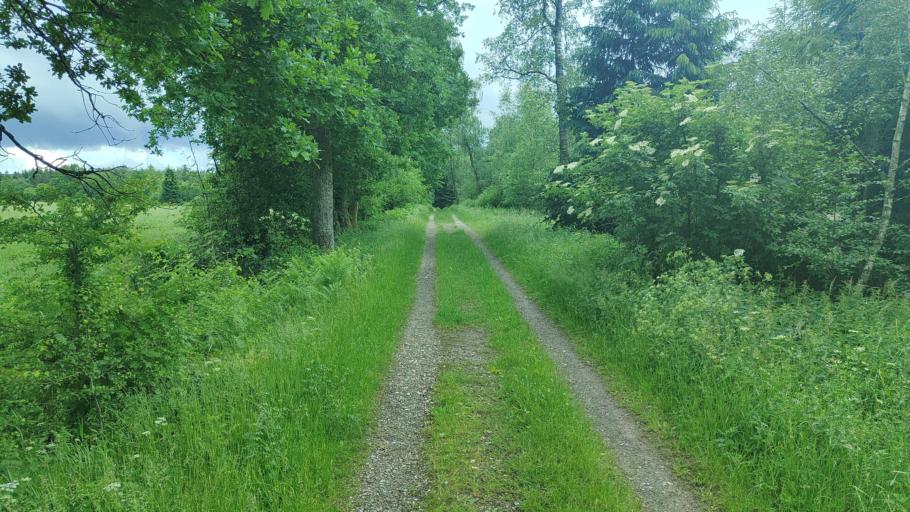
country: DE
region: North Rhine-Westphalia
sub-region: Regierungsbezirk Koln
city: Roetgen
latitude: 50.6269
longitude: 6.1758
